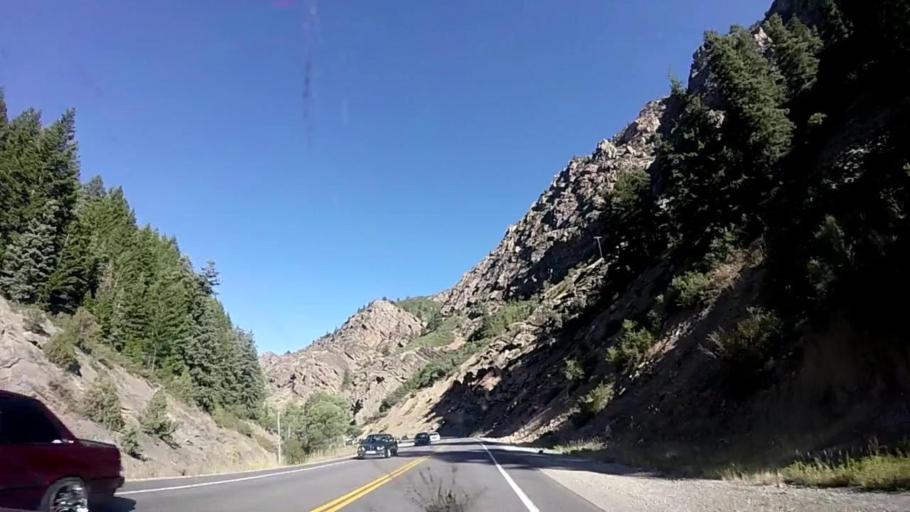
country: US
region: Utah
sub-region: Salt Lake County
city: Mount Olympus
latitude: 40.6332
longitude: -111.7065
